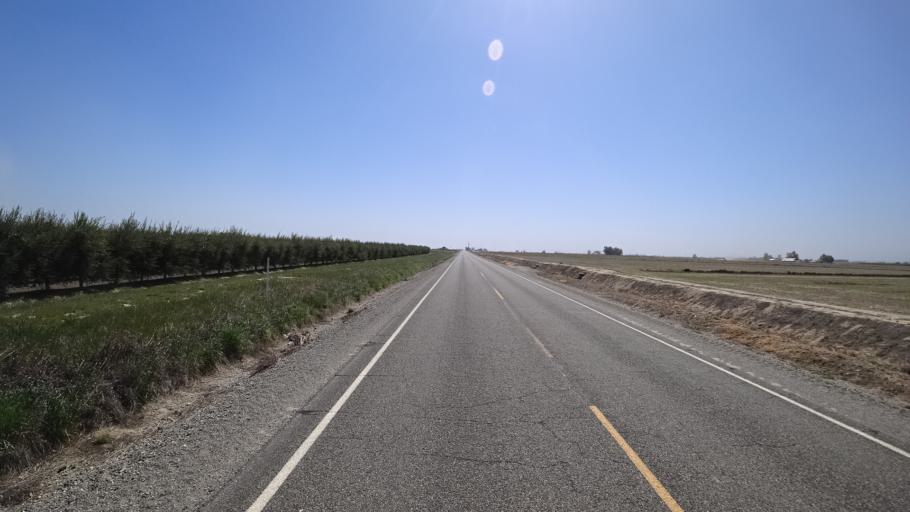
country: US
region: California
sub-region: Glenn County
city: Willows
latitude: 39.5623
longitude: -122.1369
